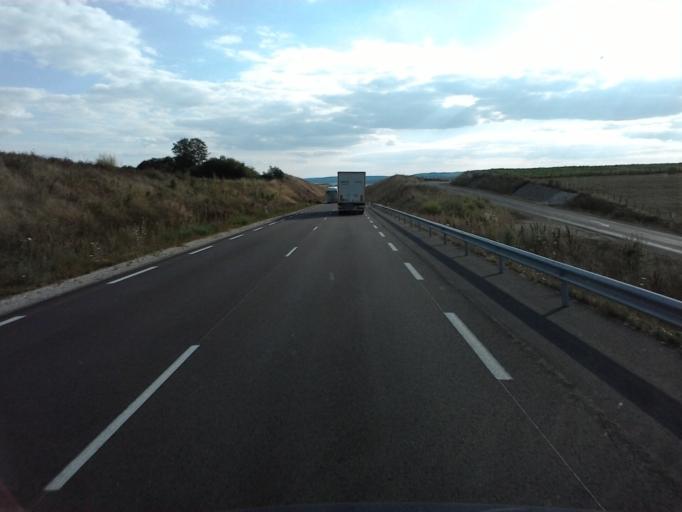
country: FR
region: Franche-Comte
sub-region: Departement de la Haute-Saone
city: Frotey-les-Vesoul
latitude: 47.7002
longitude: 6.2795
